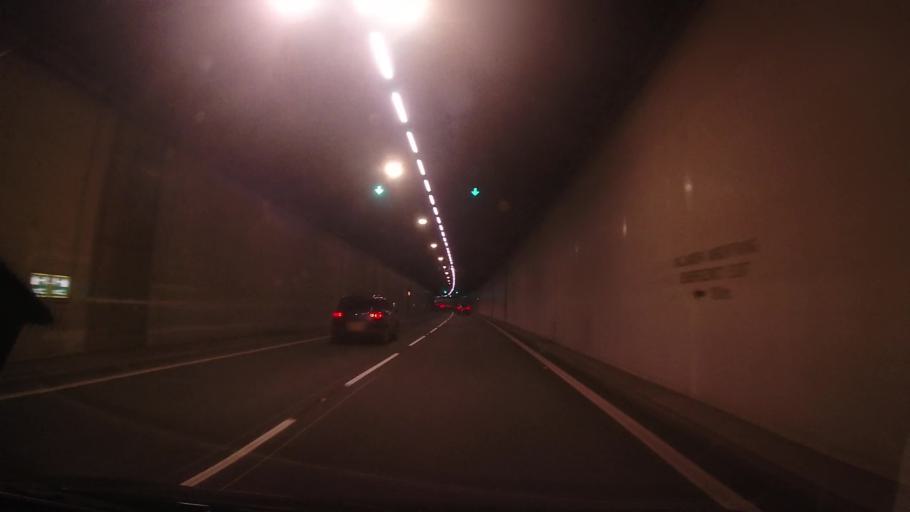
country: GB
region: Wales
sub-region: Conwy
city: Conwy
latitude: 53.2888
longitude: -3.8255
